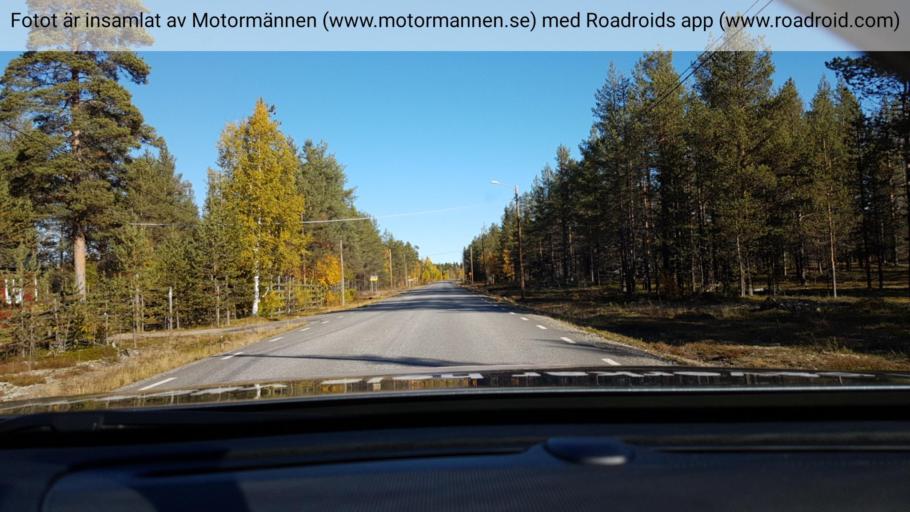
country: SE
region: Norrbotten
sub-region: Gallivare Kommun
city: Gaellivare
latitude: 66.7570
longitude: 21.0137
